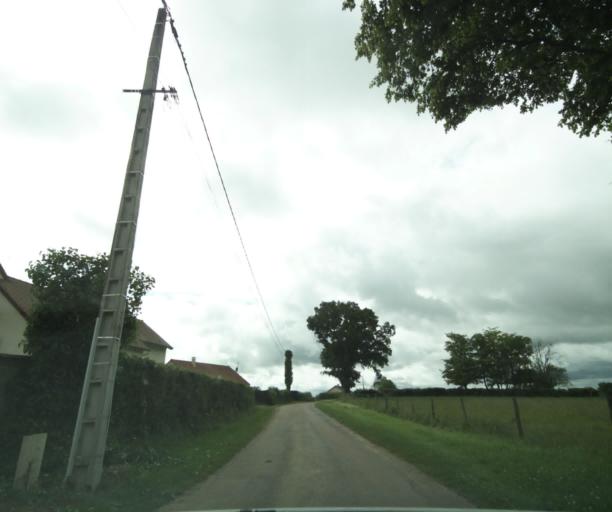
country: FR
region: Bourgogne
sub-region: Departement de Saone-et-Loire
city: Charolles
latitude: 46.4228
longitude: 4.3030
